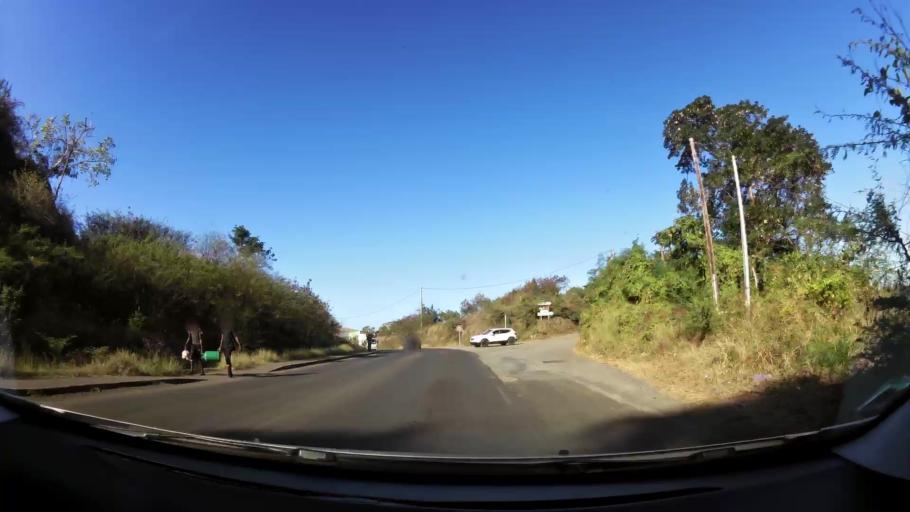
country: YT
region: Mamoudzou
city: Mamoudzou
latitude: -12.7594
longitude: 45.2297
